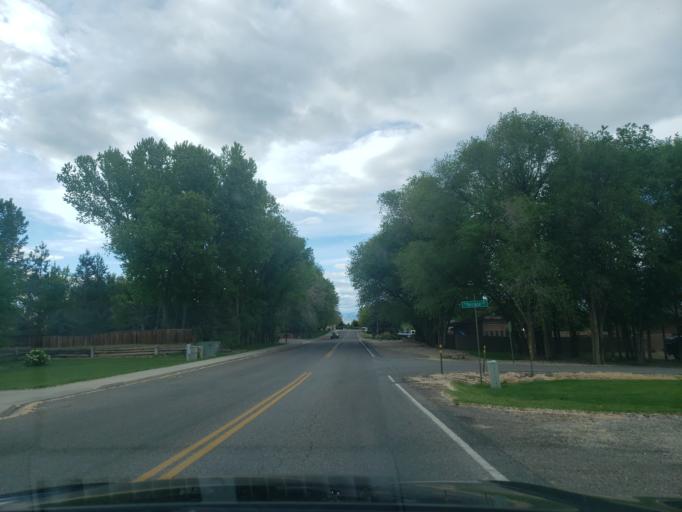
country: US
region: Colorado
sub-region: Mesa County
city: Redlands
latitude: 39.1005
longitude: -108.6687
